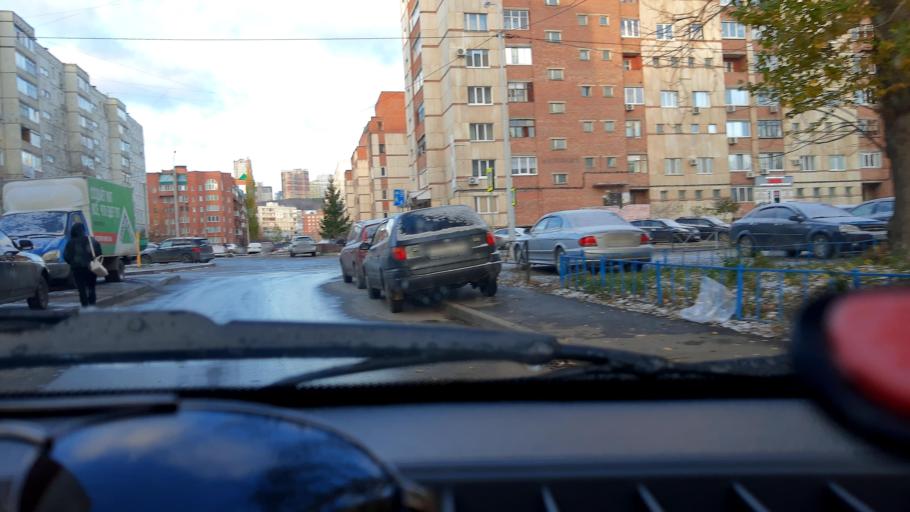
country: RU
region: Bashkortostan
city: Ufa
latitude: 54.7632
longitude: 56.0572
